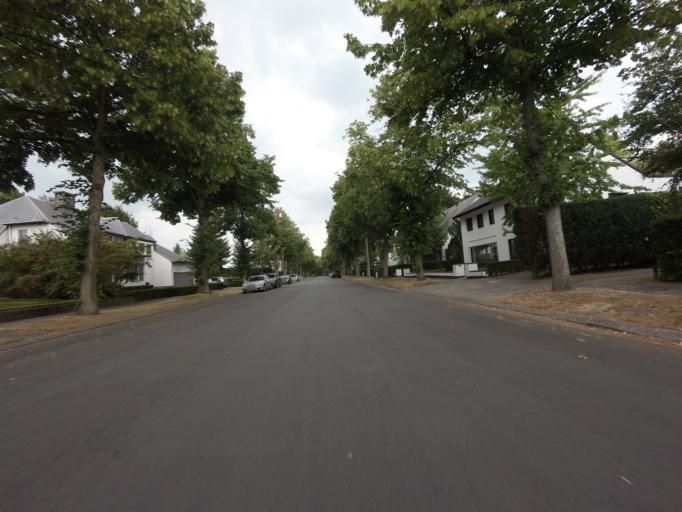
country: BE
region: Flanders
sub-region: Provincie Antwerpen
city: Edegem
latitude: 51.1699
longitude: 4.4197
